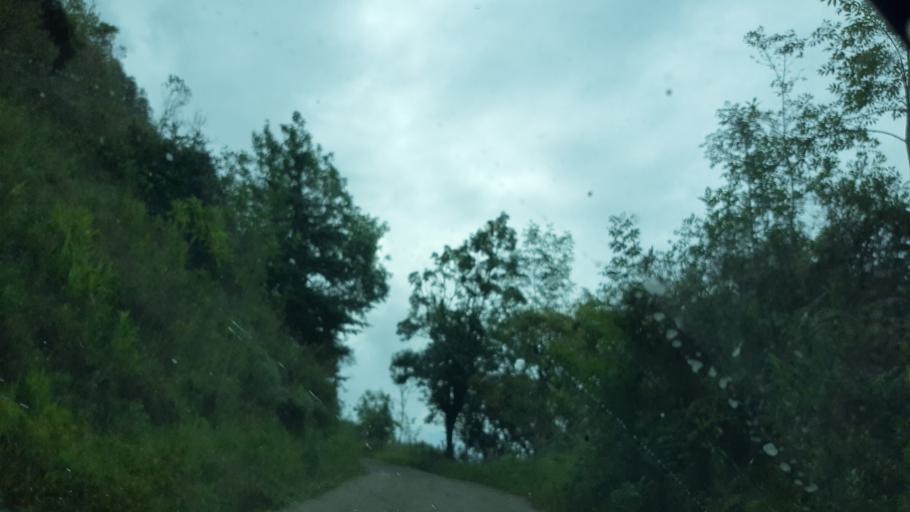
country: CO
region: Boyaca
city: Guateque
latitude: 5.0332
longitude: -73.4439
